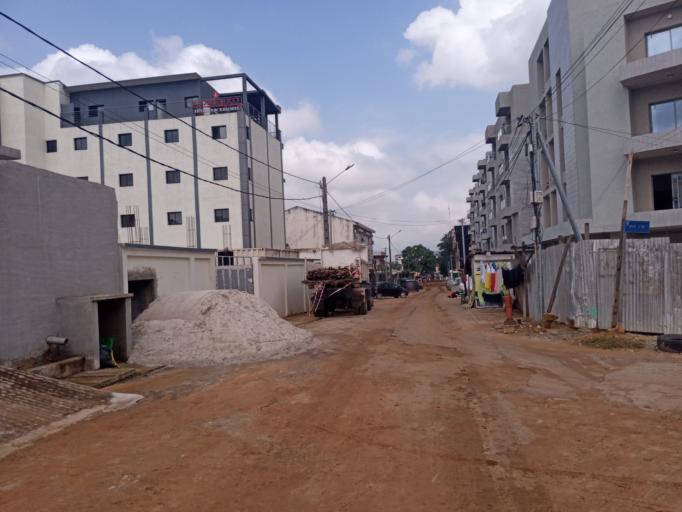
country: CI
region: Lagunes
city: Bingerville
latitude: 5.3630
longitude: -3.9574
